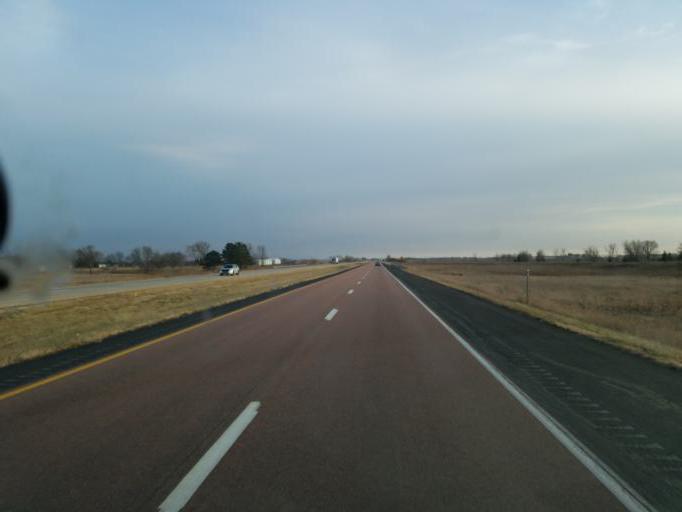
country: US
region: Iowa
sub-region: Monona County
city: Onawa
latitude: 42.0266
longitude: -96.1324
